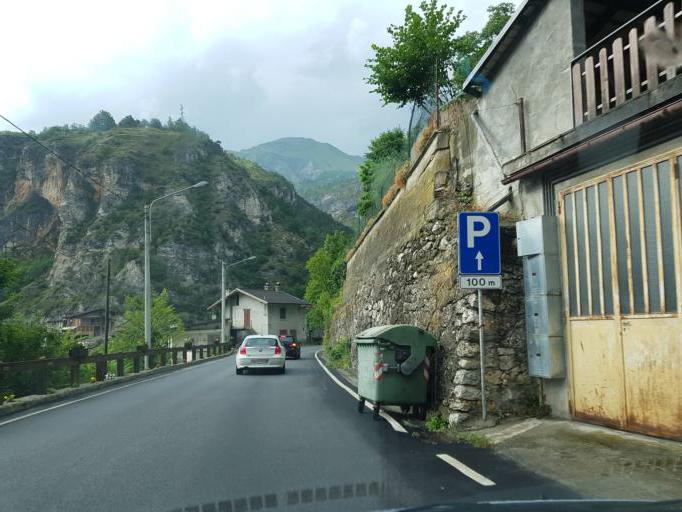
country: IT
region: Piedmont
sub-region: Provincia di Cuneo
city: Macra
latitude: 44.4987
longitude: 7.1794
